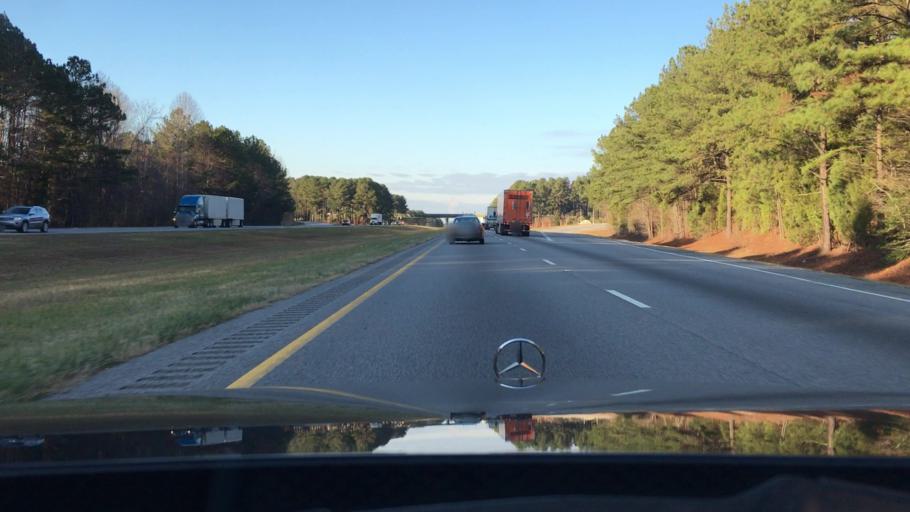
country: US
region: South Carolina
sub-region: Chester County
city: Eureka Mill
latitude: 34.7405
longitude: -81.0349
